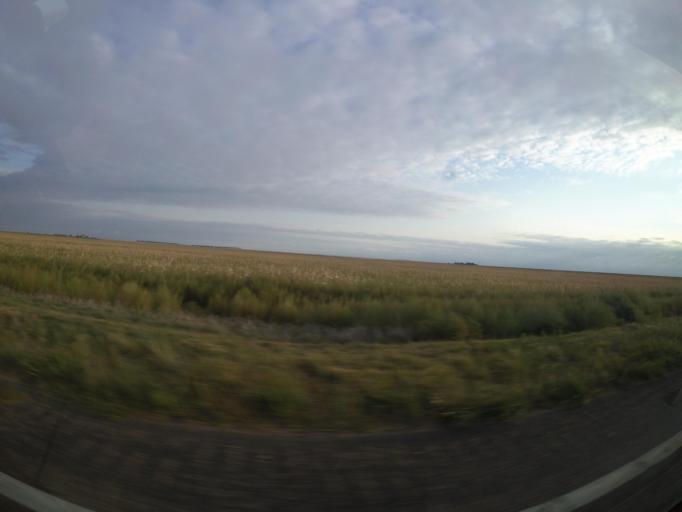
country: US
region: Colorado
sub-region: Yuma County
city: Wray
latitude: 39.7026
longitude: -102.2706
